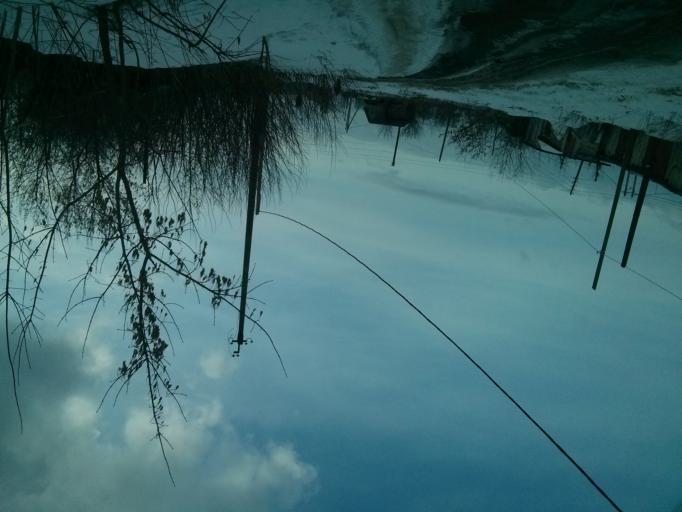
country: RU
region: Nizjnij Novgorod
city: Afonino
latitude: 56.2725
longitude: 44.0330
